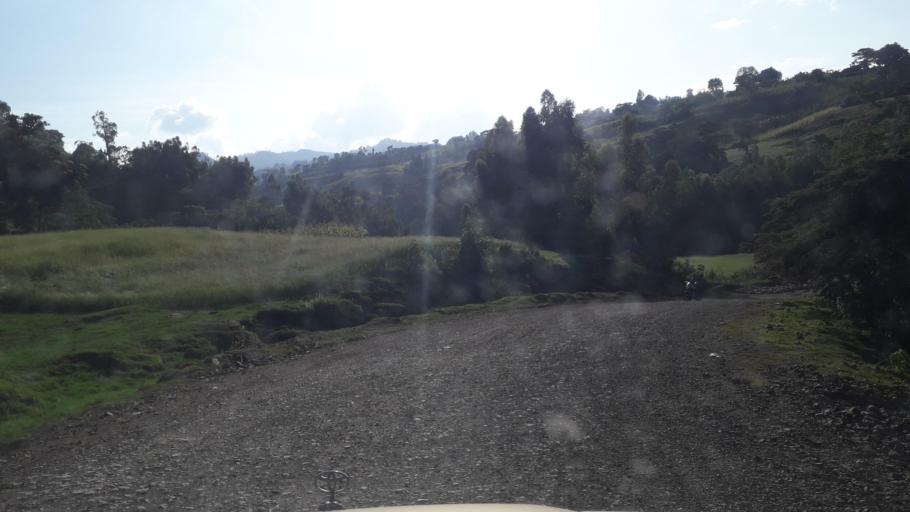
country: ET
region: Oromiya
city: Jima
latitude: 7.4761
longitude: 36.8770
